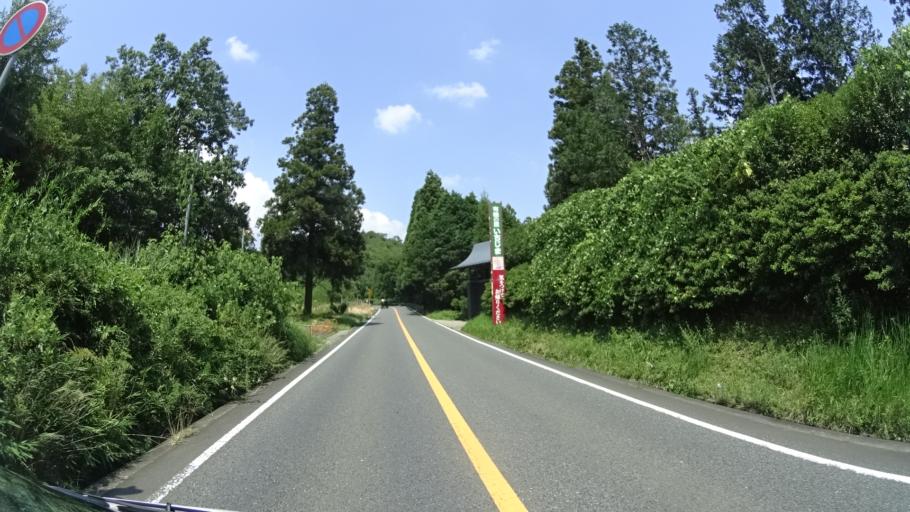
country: JP
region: Kyoto
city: Fukuchiyama
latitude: 35.2605
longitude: 135.1464
